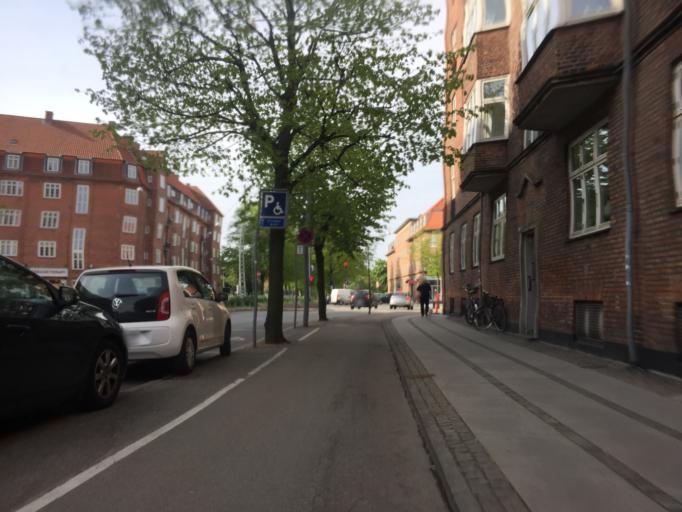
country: DK
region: Capital Region
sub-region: Kobenhavn
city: Vanlose
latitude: 55.6794
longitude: 12.5094
